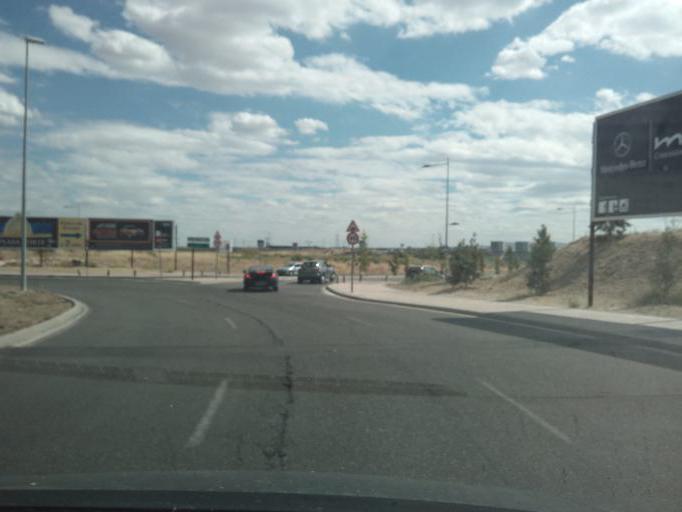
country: ES
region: Madrid
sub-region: Provincia de Madrid
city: San Sebastian de los Reyes
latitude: 40.5656
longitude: -3.6067
